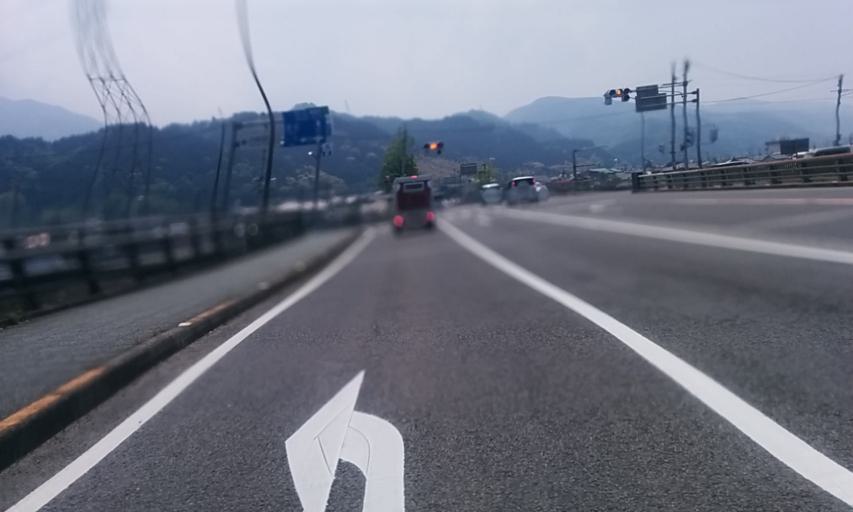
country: JP
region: Ehime
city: Saijo
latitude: 33.9027
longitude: 133.1837
